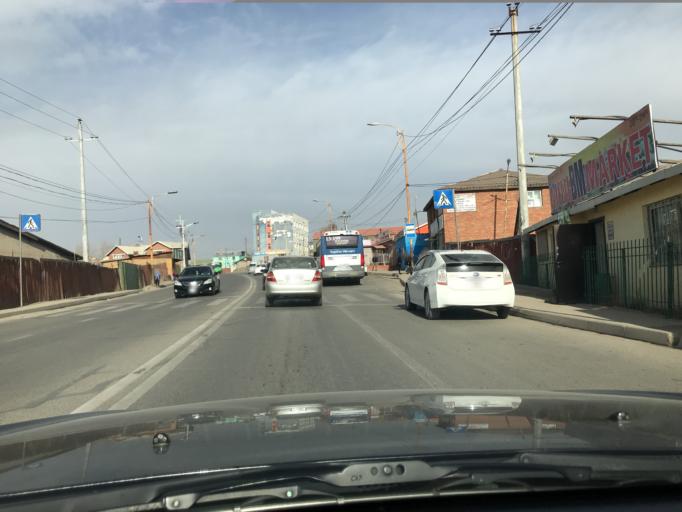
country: MN
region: Ulaanbaatar
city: Ulaanbaatar
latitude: 47.9328
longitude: 106.8872
